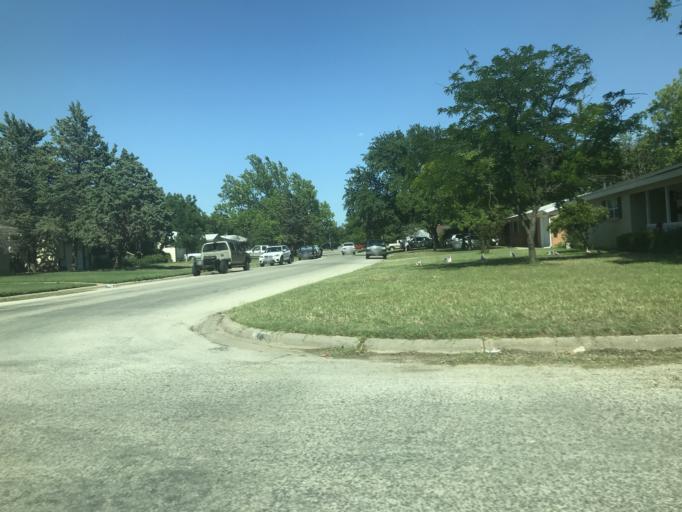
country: US
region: Texas
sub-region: Taylor County
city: Abilene
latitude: 32.4097
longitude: -99.7511
